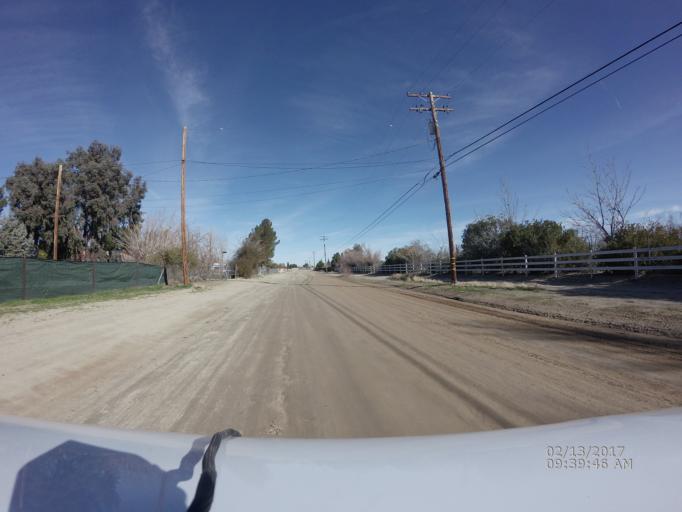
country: US
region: California
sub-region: Los Angeles County
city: Littlerock
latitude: 34.5544
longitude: -117.9670
